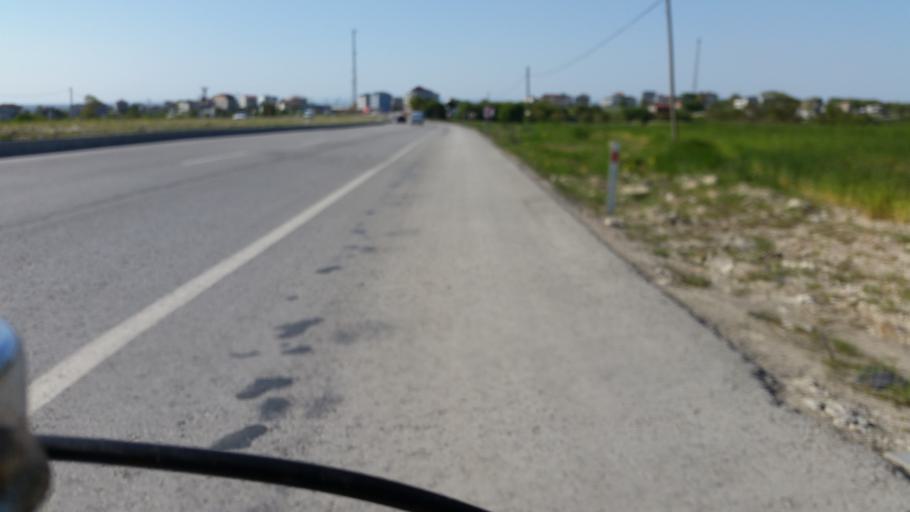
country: TR
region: Tekirdag
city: Cerkezkoey
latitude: 41.3520
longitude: 27.9570
